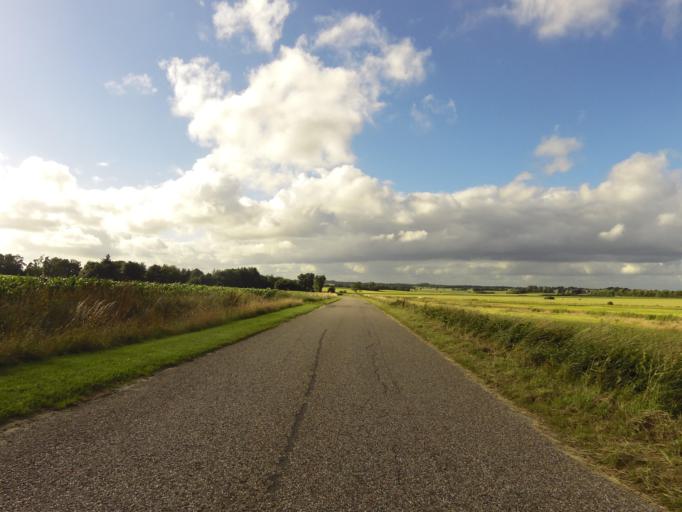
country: DK
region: South Denmark
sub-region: Tonder Kommune
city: Toftlund
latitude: 55.1568
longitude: 9.0860
